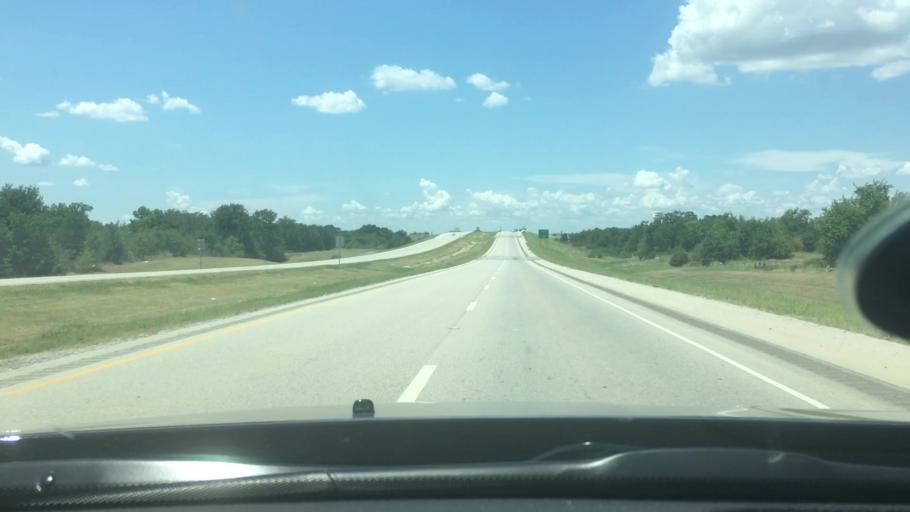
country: US
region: Oklahoma
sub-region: Bryan County
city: Durant
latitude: 33.9656
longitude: -96.3875
